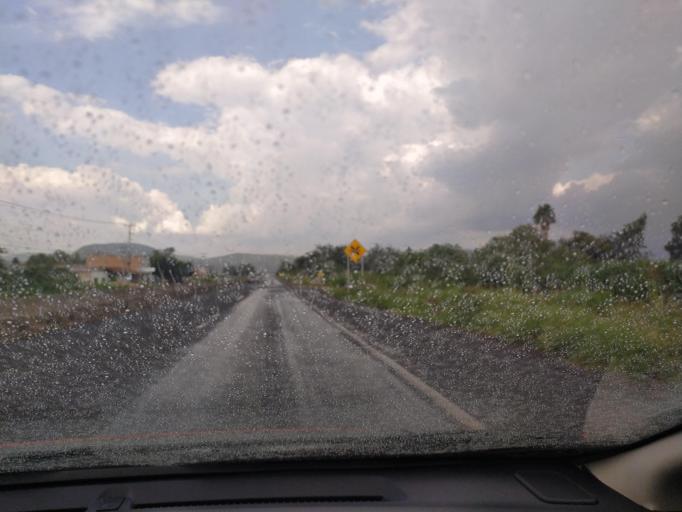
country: MX
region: Jalisco
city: Bellavista
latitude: 20.4181
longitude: -103.6223
